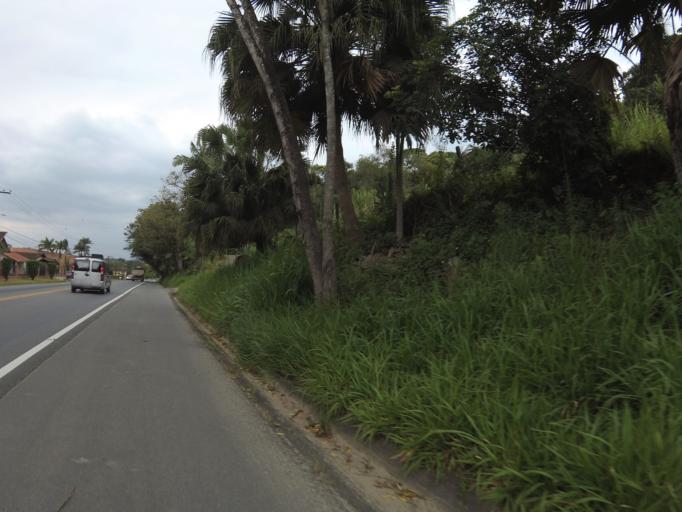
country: BR
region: Santa Catarina
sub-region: Indaial
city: Indaial
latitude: -26.8428
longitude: -49.1615
